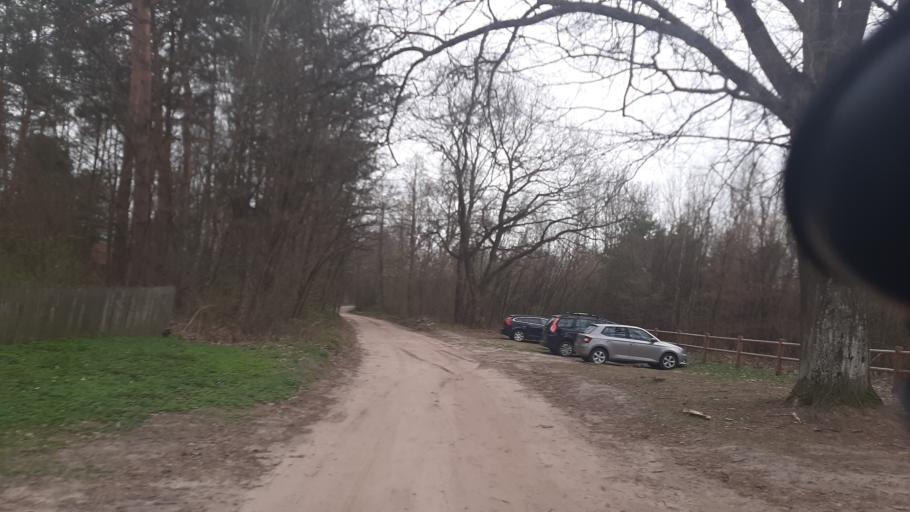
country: PL
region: Lublin Voivodeship
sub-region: Powiat lubelski
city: Niemce
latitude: 51.3892
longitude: 22.5650
